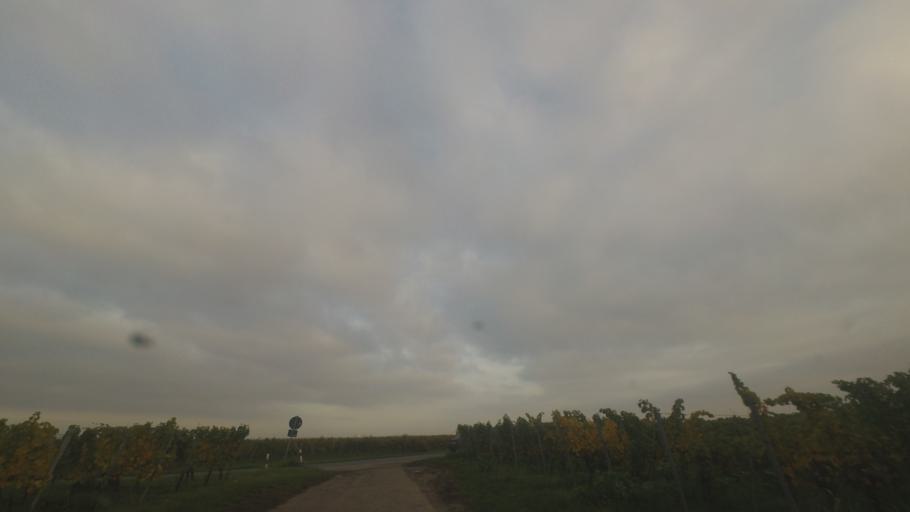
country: DE
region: Rheinland-Pfalz
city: Bechtheim
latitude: 49.7142
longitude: 8.3067
